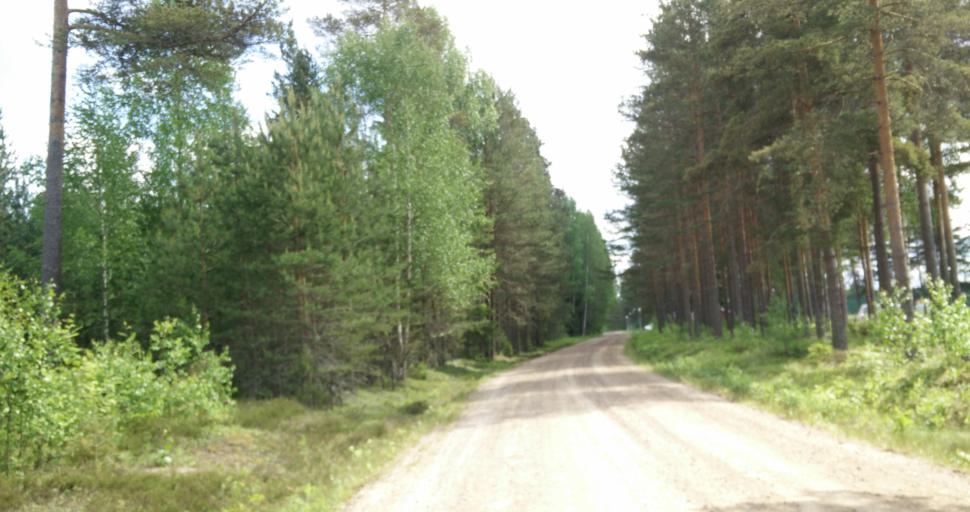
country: SE
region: Vaermland
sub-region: Hagfors Kommun
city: Hagfors
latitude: 60.0101
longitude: 13.5850
